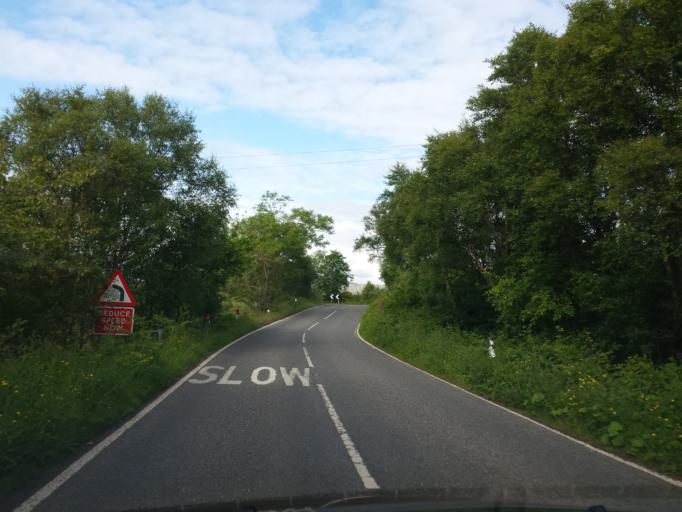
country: GB
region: Scotland
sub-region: Argyll and Bute
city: Isle Of Mull
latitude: 56.9546
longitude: -5.8429
